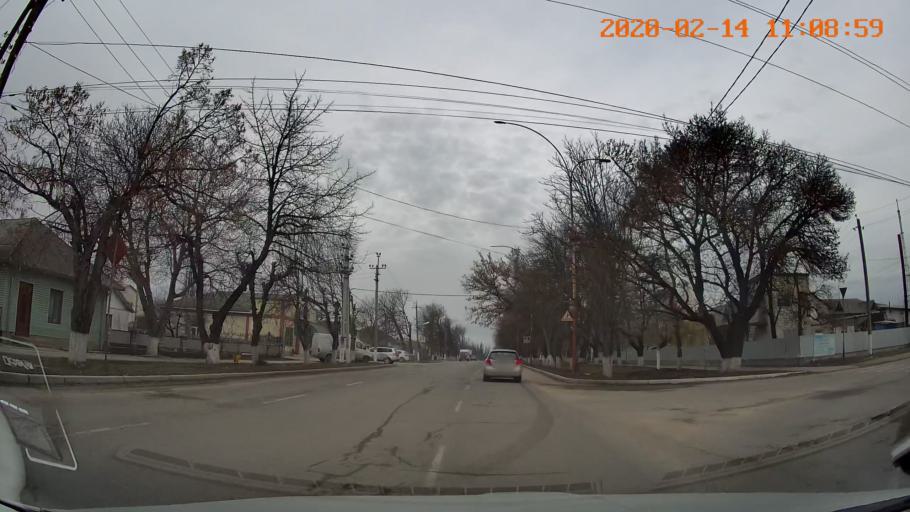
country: MD
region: Raionul Edinet
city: Edinet
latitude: 48.1754
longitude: 27.2973
